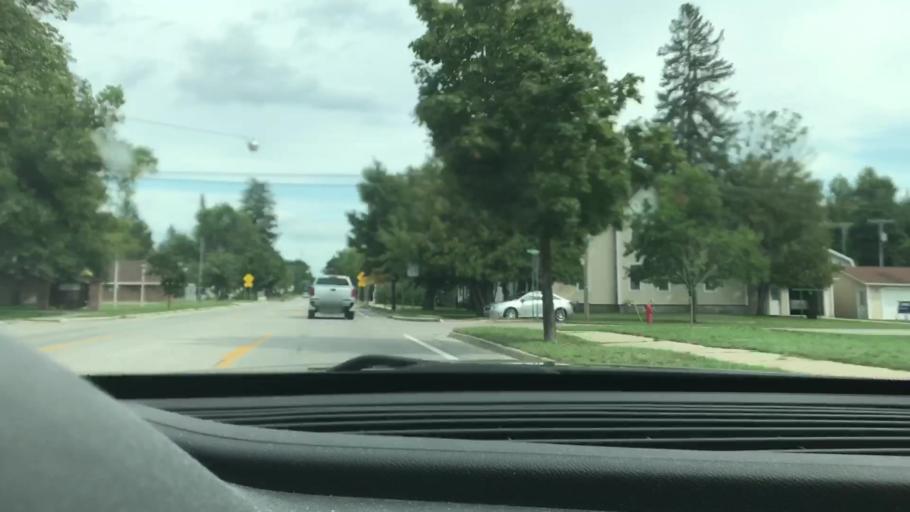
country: US
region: Michigan
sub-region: Antrim County
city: Bellaire
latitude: 44.9756
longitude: -85.2074
